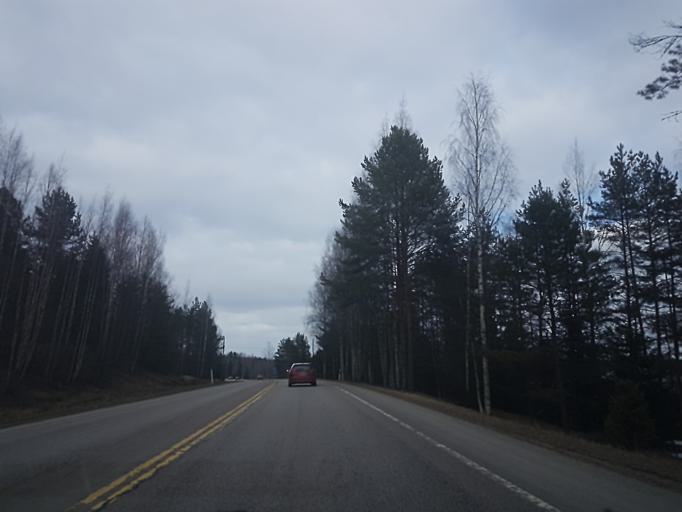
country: FI
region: South Karelia
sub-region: Imatra
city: Parikkala
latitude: 61.4788
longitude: 29.4725
